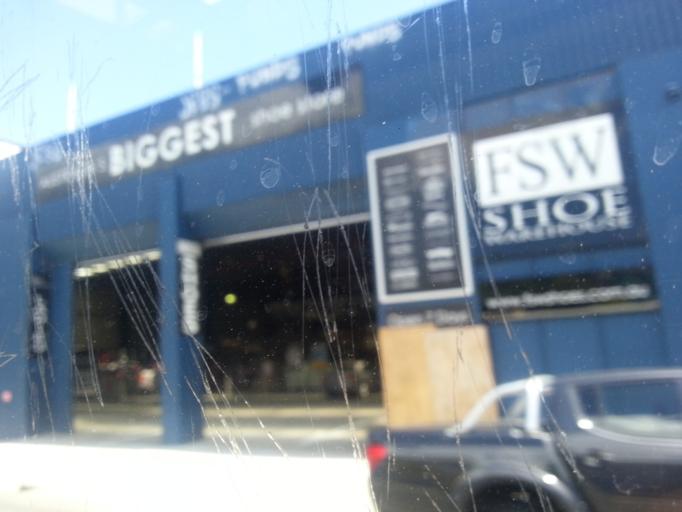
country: AU
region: New South Wales
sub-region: City of Sydney
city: Alexandria
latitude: -33.9025
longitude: 151.1967
